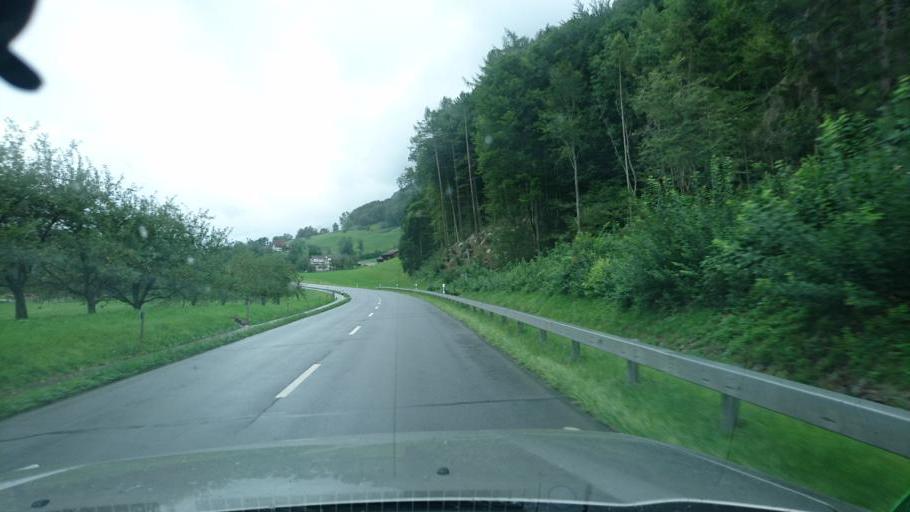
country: CH
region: Saint Gallen
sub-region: Wahlkreis Sarganserland
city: Flums
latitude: 47.0788
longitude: 9.3819
